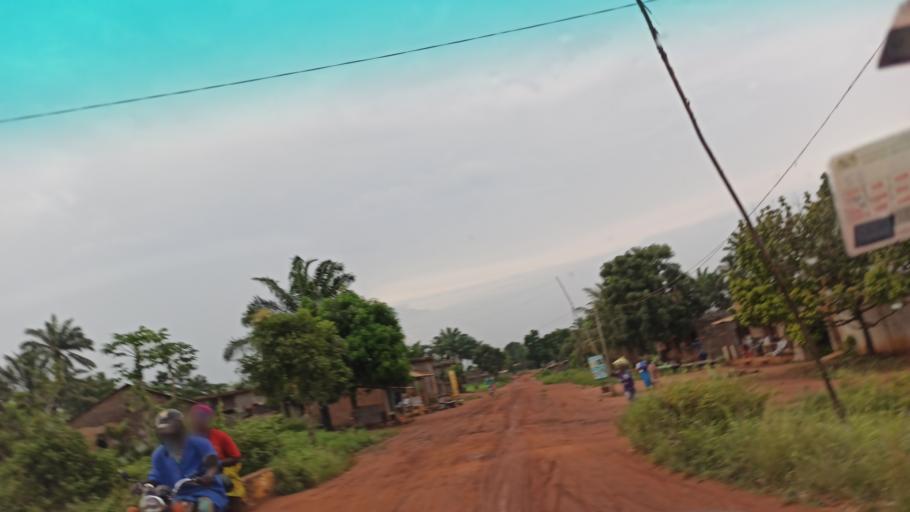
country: BJ
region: Queme
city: Porto-Novo
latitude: 6.4846
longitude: 2.6703
